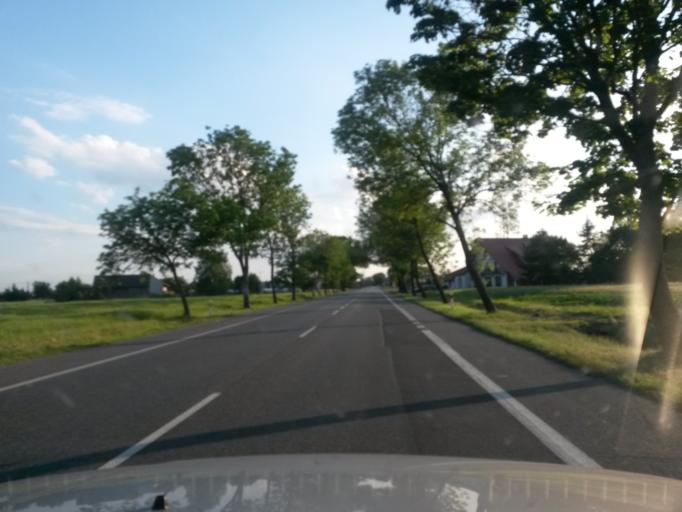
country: PL
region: Lodz Voivodeship
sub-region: Powiat wielunski
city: Wierzchlas
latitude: 51.2425
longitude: 18.6845
